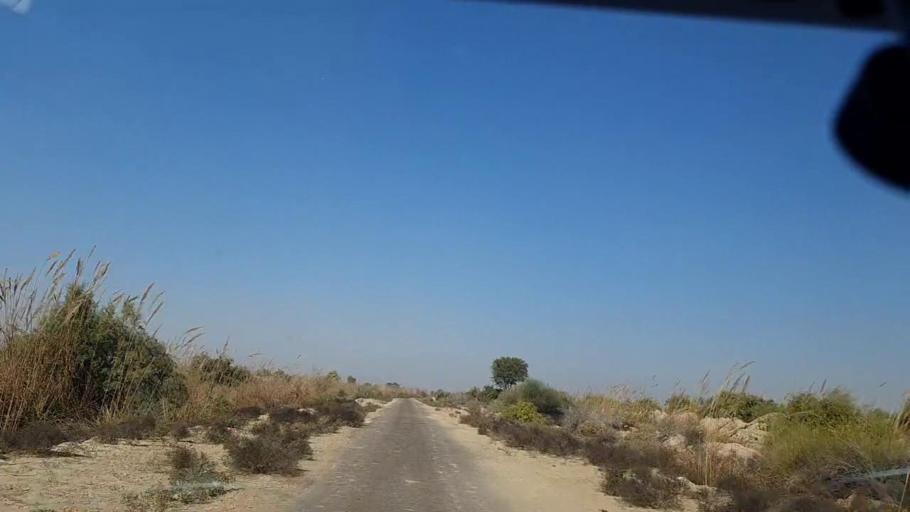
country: PK
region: Sindh
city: Khanpur
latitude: 27.5894
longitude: 69.3757
